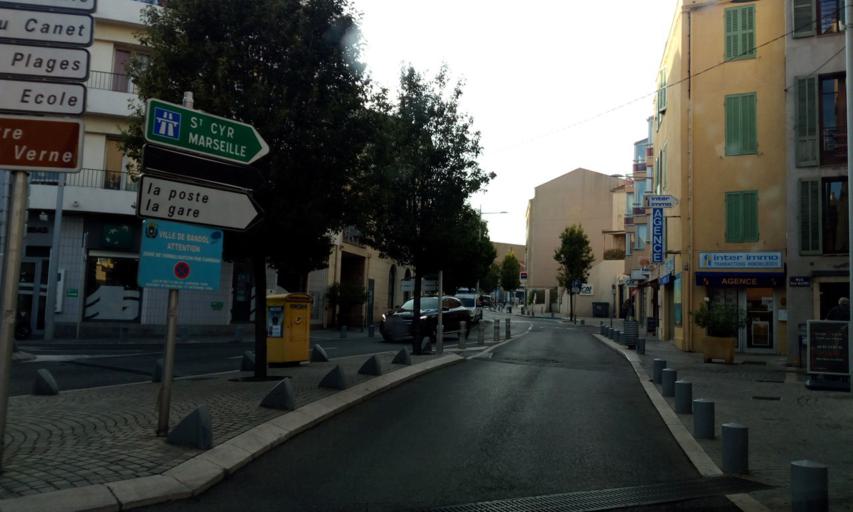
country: FR
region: Provence-Alpes-Cote d'Azur
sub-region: Departement du Var
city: Bandol
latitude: 43.1361
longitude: 5.7536
